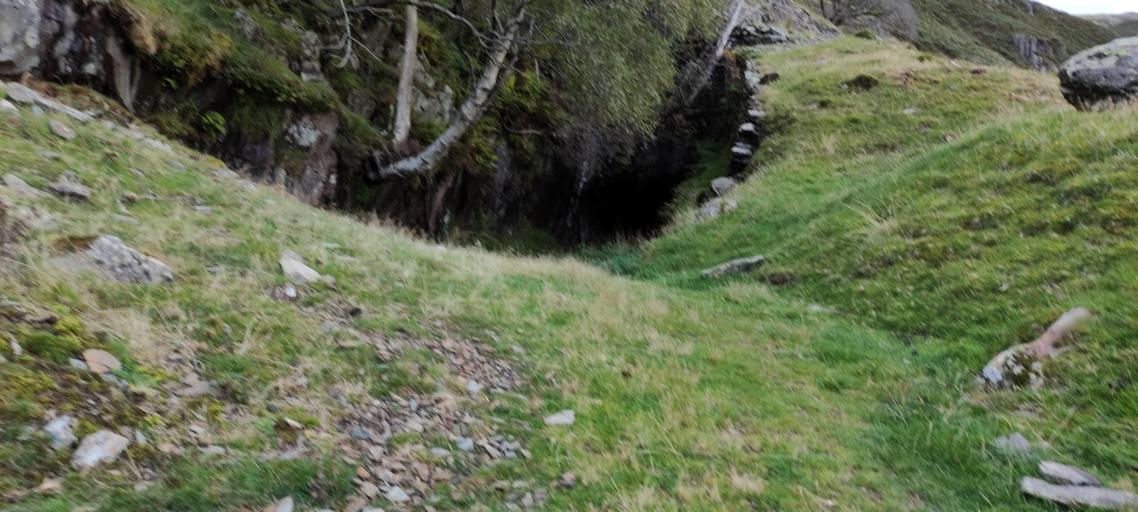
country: GB
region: England
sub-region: Cumbria
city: Ambleside
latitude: 54.3820
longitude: -3.0966
